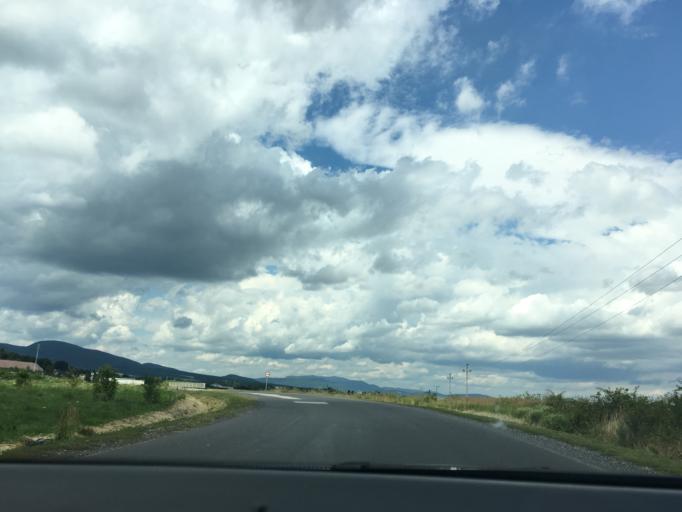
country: HU
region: Borsod-Abauj-Zemplen
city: Satoraljaujhely
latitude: 48.4064
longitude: 21.6619
